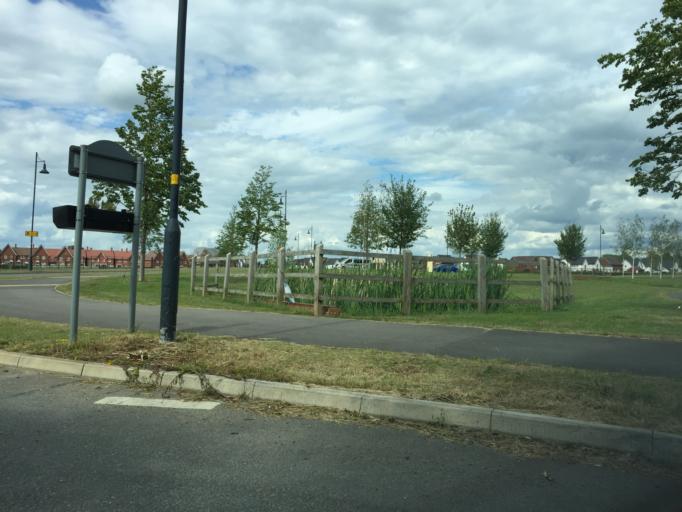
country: GB
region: England
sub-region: Wiltshire
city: Purton
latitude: 51.6054
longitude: -1.8286
